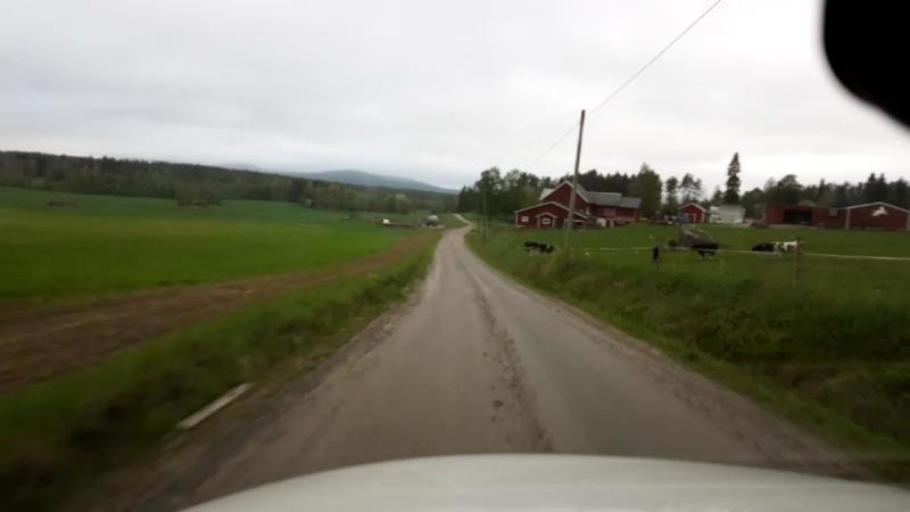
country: SE
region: Gaevleborg
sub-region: Ljusdals Kommun
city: Jaervsoe
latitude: 61.7759
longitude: 16.2077
